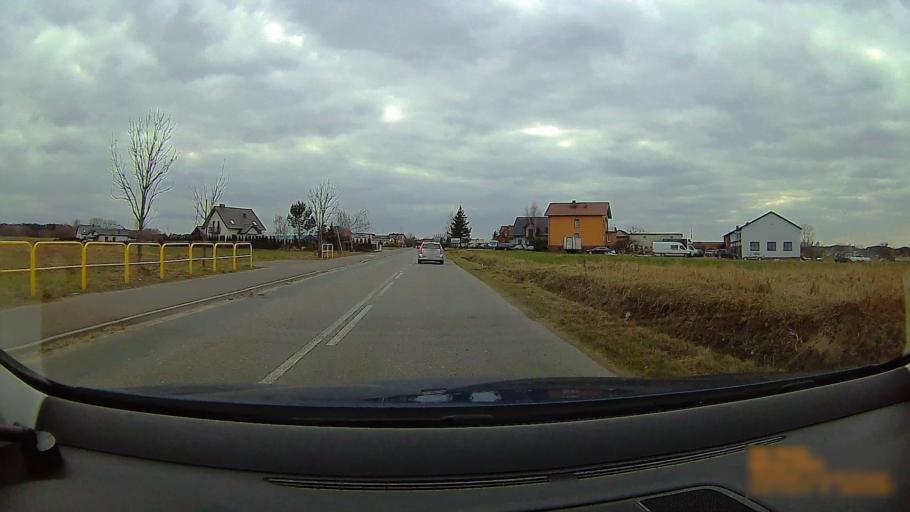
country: PL
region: Greater Poland Voivodeship
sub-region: Powiat koninski
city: Golina
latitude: 52.1909
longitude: 18.1181
